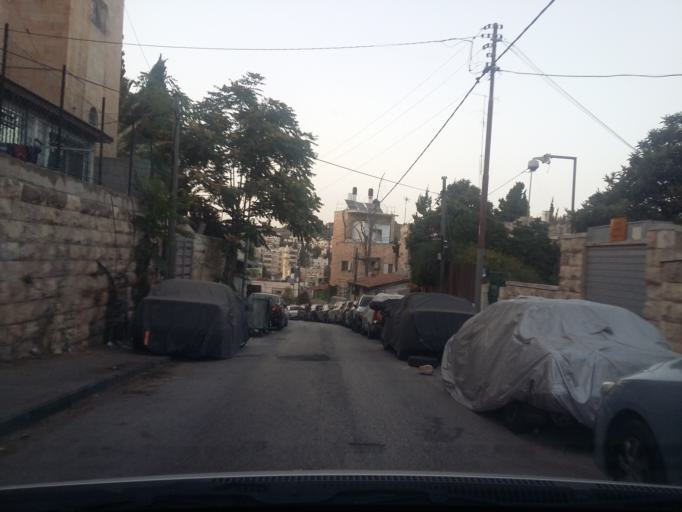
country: PS
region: West Bank
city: East Jerusalem
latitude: 31.7864
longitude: 35.2363
